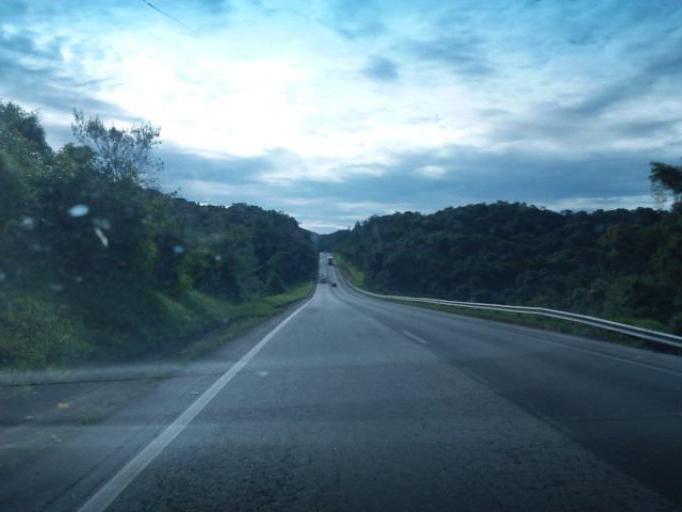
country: BR
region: Parana
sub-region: Antonina
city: Antonina
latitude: -25.1077
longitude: -48.7774
